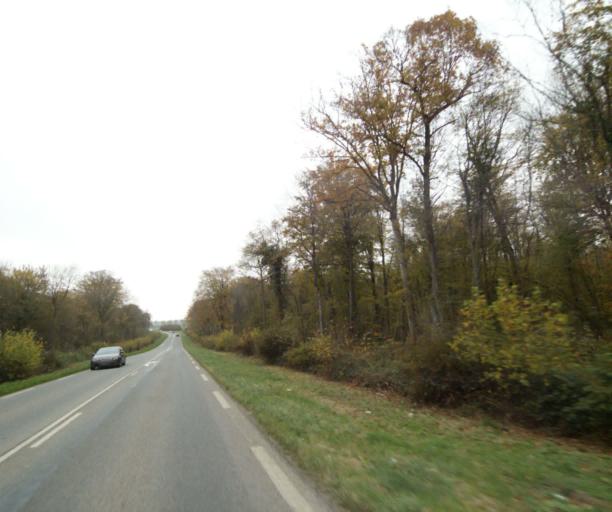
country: FR
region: Lorraine
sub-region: Departement de Meurthe-et-Moselle
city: Moutiers
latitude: 49.2428
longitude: 5.9659
